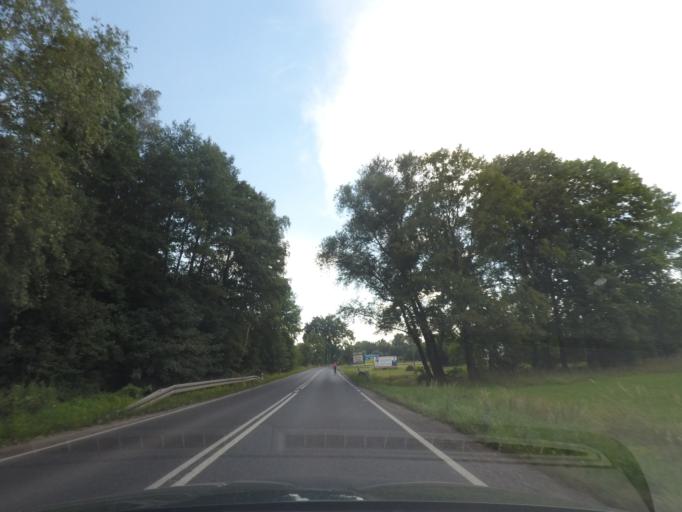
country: PL
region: Lesser Poland Voivodeship
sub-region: Powiat oswiecimski
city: Przecieszyn
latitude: 49.9938
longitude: 19.1697
